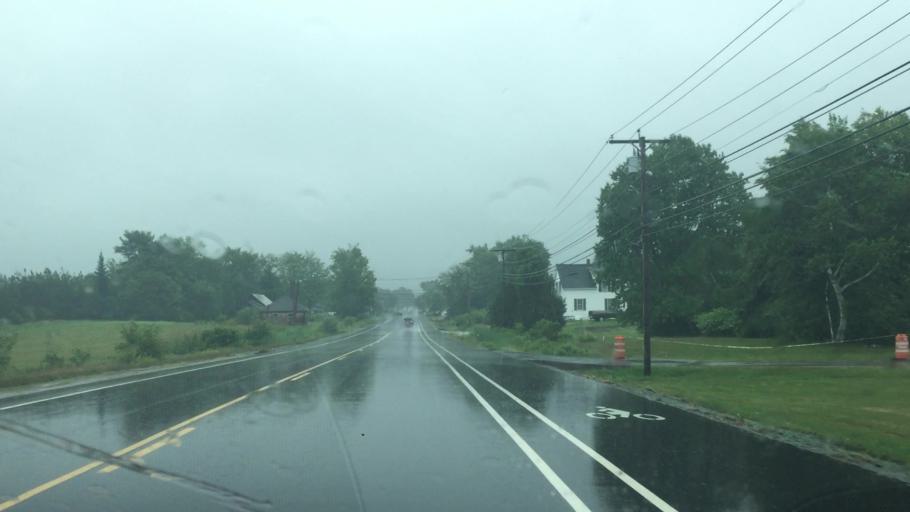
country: US
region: Maine
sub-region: Cumberland County
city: Freeport
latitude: 43.8232
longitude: -70.1394
